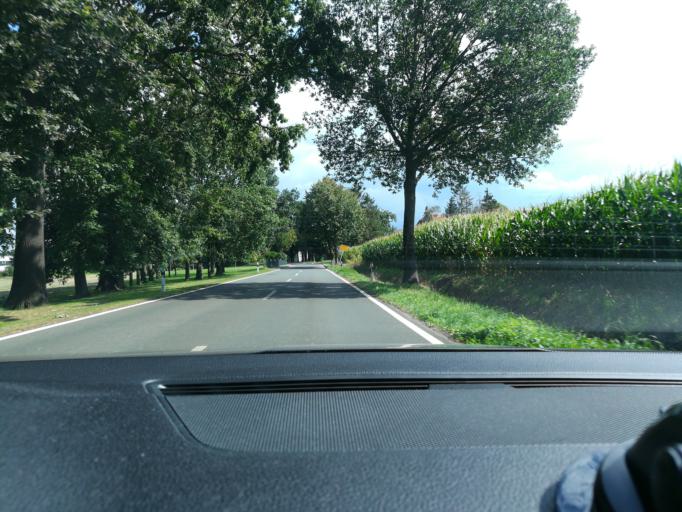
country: DE
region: North Rhine-Westphalia
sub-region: Regierungsbezirk Detmold
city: Hille
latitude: 52.3374
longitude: 8.7940
